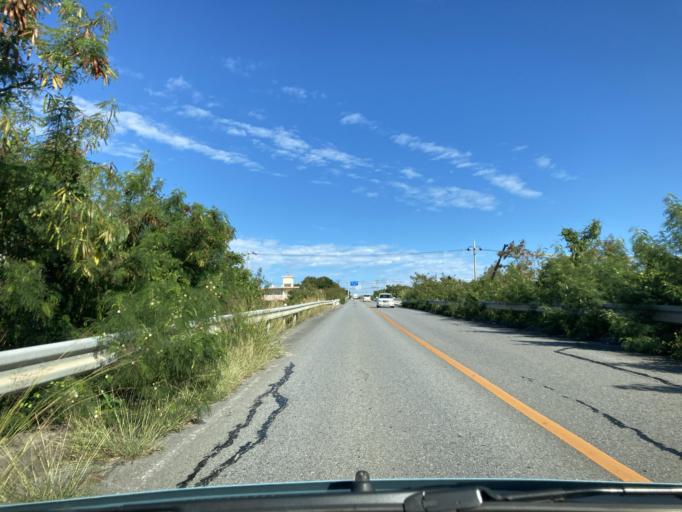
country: JP
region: Okinawa
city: Okinawa
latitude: 26.3799
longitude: 127.7455
